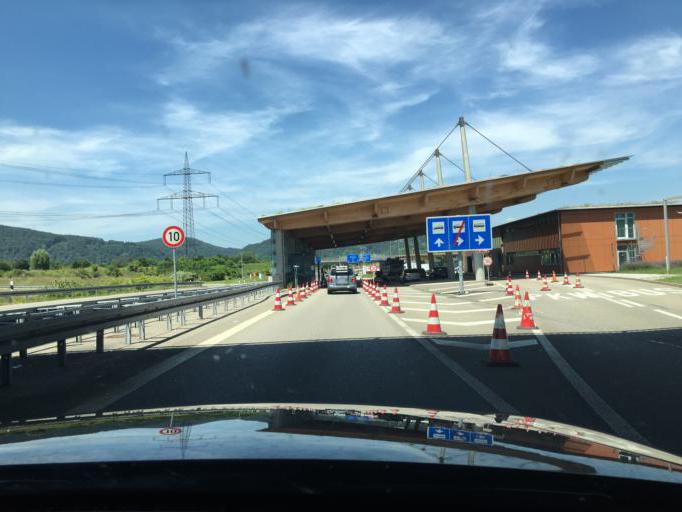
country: DE
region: Baden-Wuerttemberg
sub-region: Freiburg Region
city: Rheinfelden (Baden)
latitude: 47.5503
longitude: 7.7579
